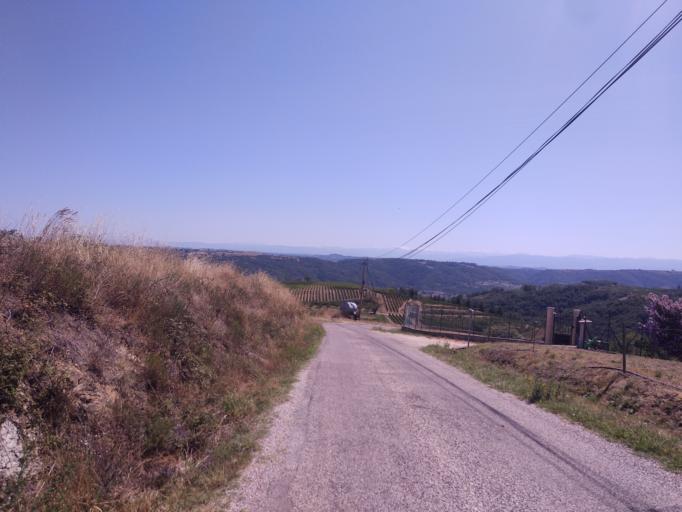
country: FR
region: Rhone-Alpes
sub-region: Departement de l'Ardeche
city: Sarras
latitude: 45.1864
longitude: 4.7789
